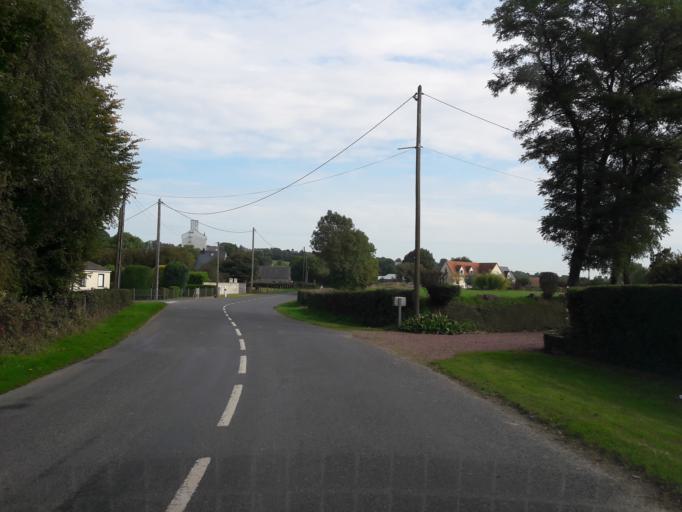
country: FR
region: Lower Normandy
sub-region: Departement du Calvados
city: Cahagnes
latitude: 49.0802
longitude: -0.8154
